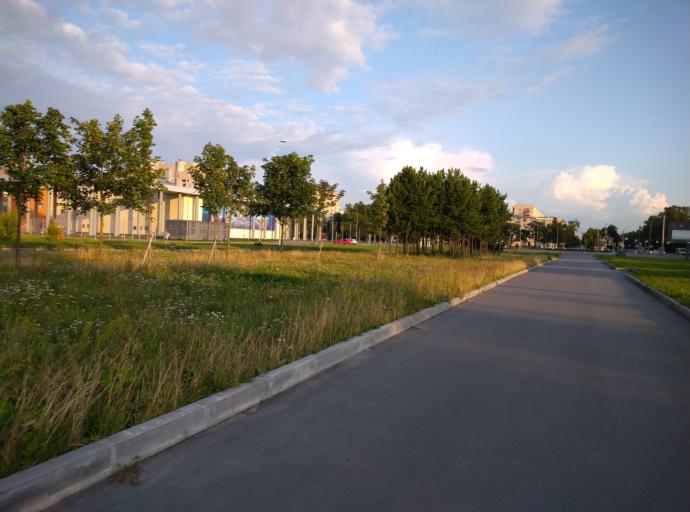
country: RU
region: St.-Petersburg
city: Kupchino
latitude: 59.8666
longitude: 30.3374
